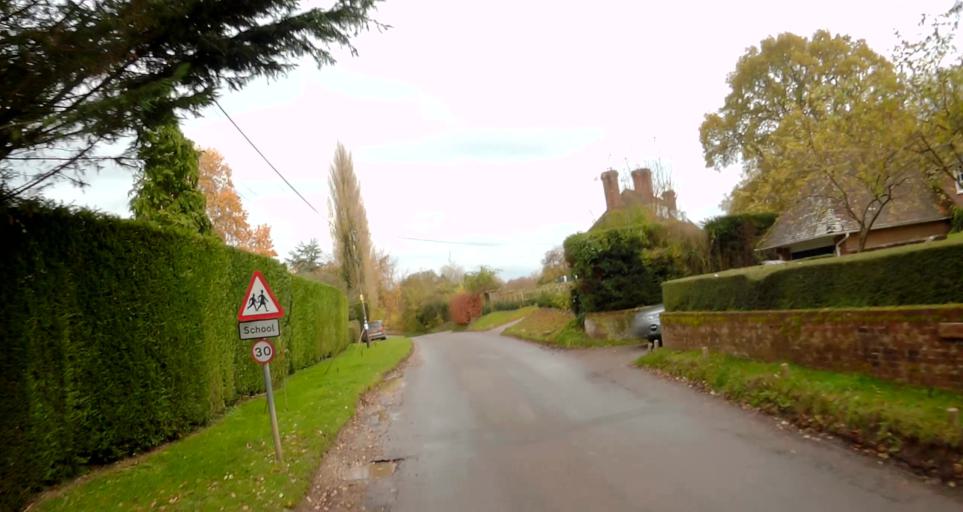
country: GB
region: England
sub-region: Hampshire
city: Long Sutton
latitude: 51.2199
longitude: -0.9405
